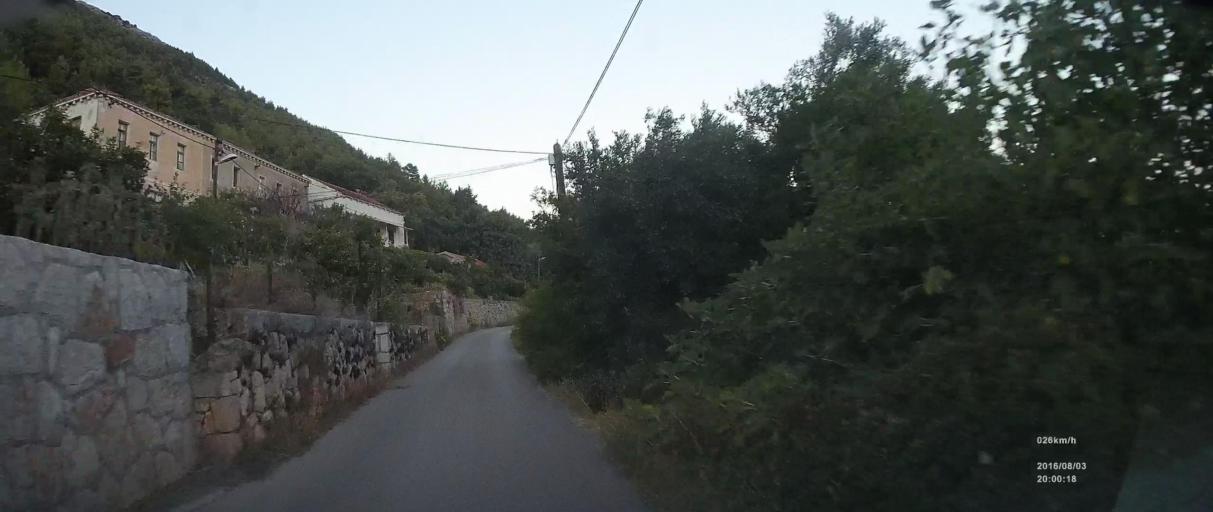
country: HR
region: Dubrovacko-Neretvanska
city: Blato
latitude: 42.7322
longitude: 17.5628
